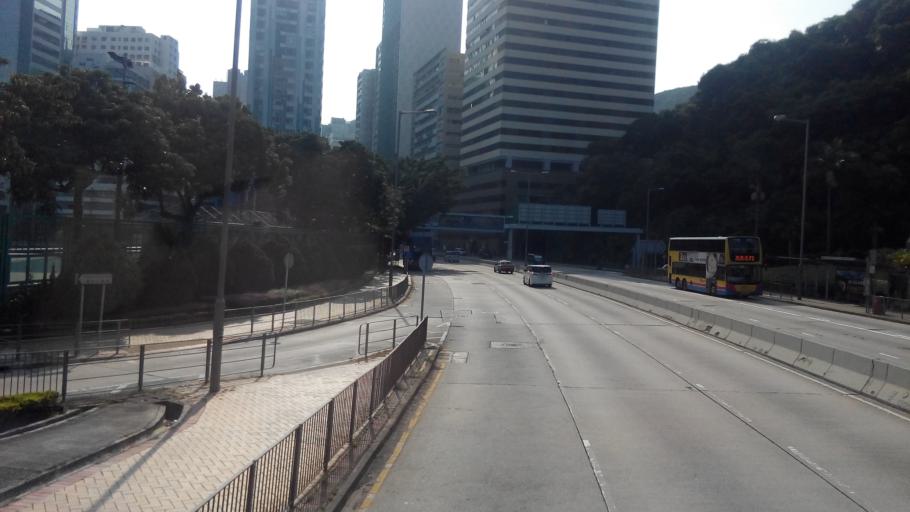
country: HK
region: Wanchai
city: Wan Chai
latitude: 22.2503
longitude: 114.1710
